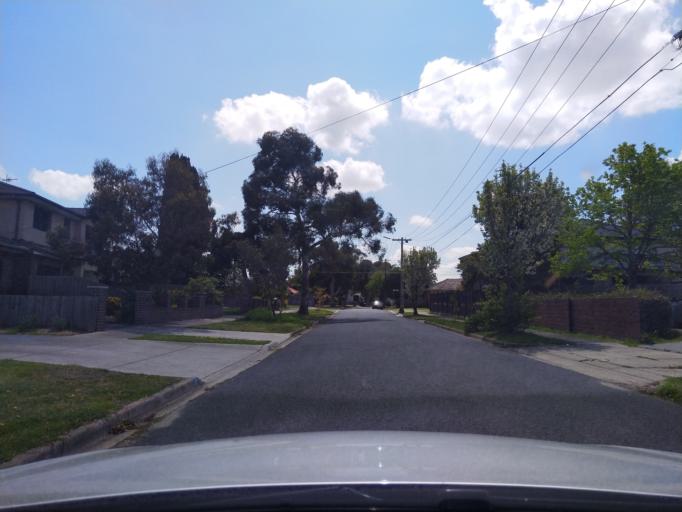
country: AU
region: Victoria
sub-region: Banyule
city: Bellfield
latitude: -37.7530
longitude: 145.0415
